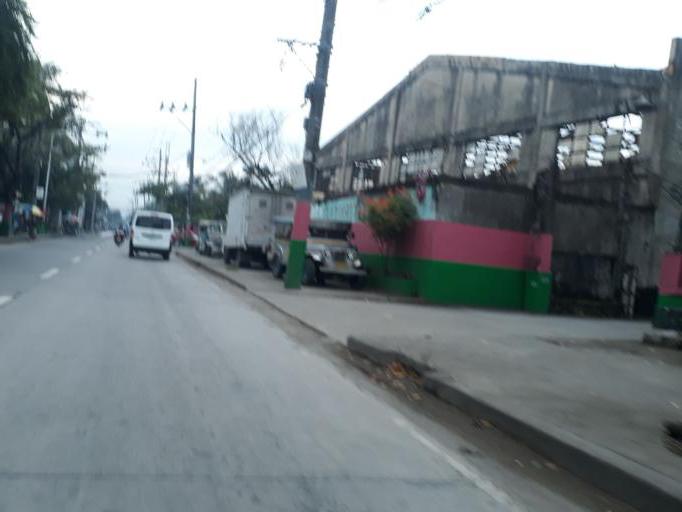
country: PH
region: Calabarzon
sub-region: Province of Rizal
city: Valenzuela
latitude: 14.6943
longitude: 120.9548
